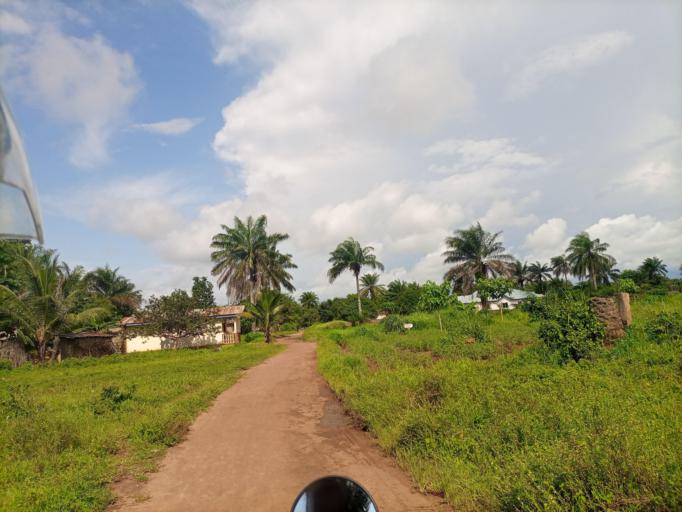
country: SL
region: Northern Province
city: Masoyila
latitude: 8.6292
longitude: -13.1824
